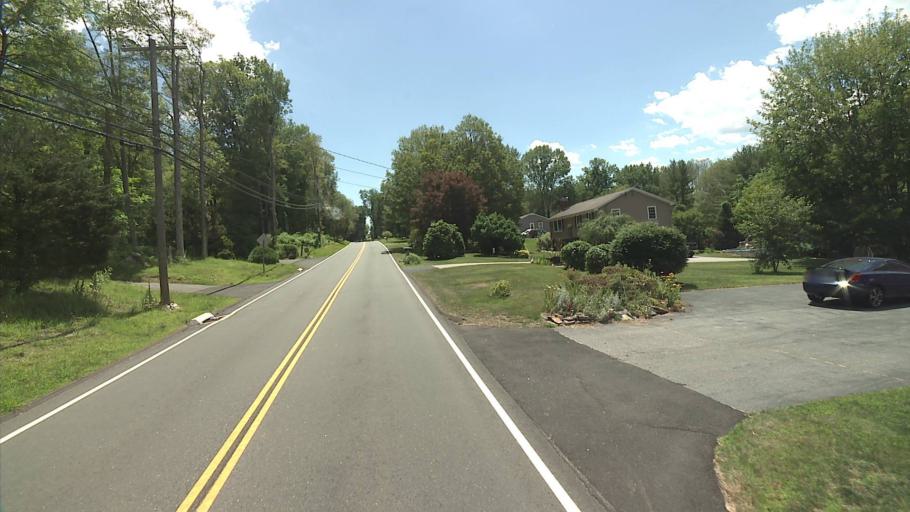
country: US
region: Connecticut
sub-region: Middlesex County
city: Moodus
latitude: 41.4908
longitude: -72.4477
